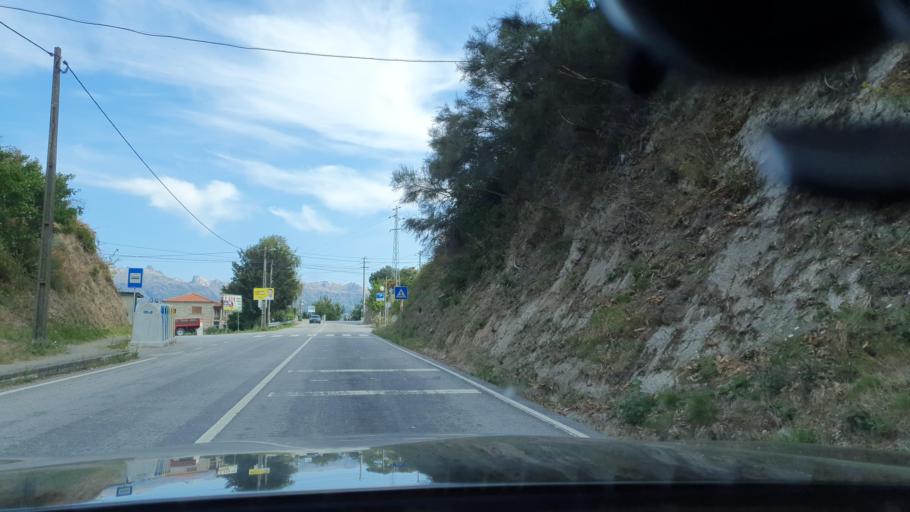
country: PT
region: Braga
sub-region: Vieira do Minho
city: Vieira do Minho
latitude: 41.6782
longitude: -8.1178
